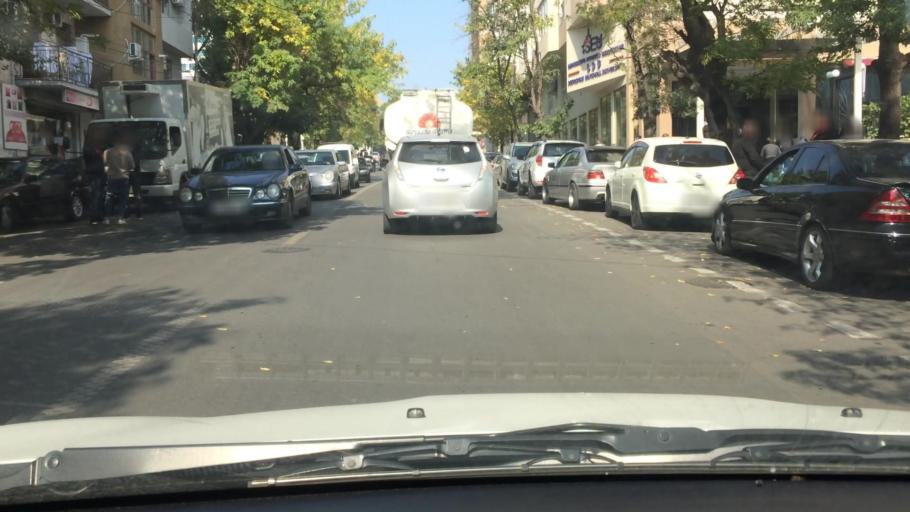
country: GE
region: T'bilisi
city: Tbilisi
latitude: 41.6891
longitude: 44.8278
